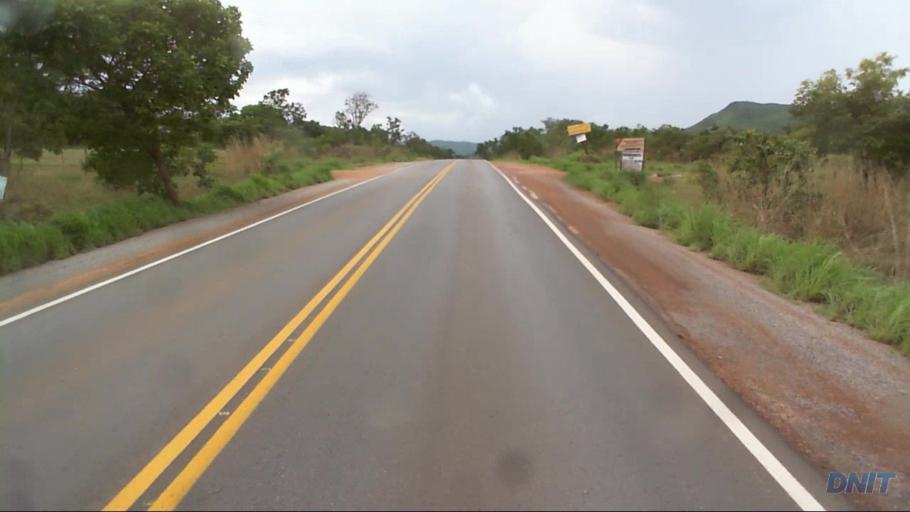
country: BR
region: Goias
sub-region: Padre Bernardo
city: Padre Bernardo
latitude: -15.4034
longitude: -48.1999
